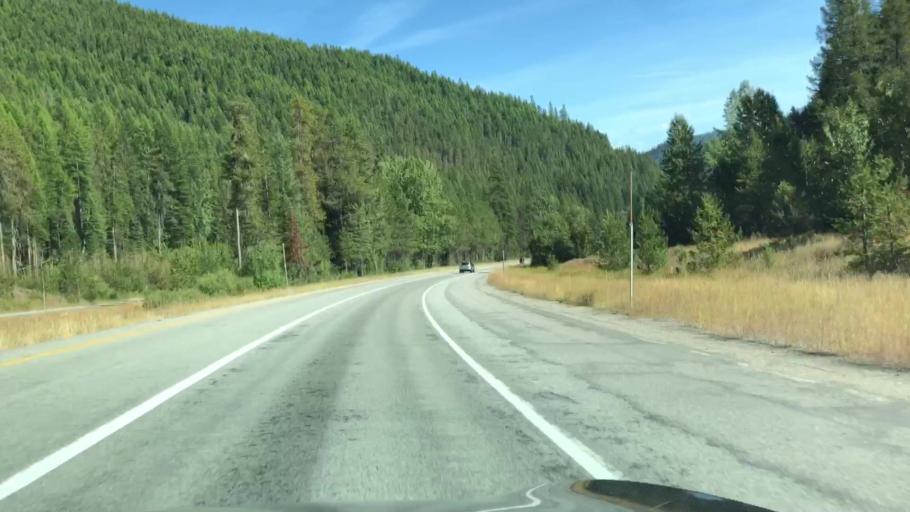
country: US
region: Idaho
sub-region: Shoshone County
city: Wallace
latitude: 47.4308
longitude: -115.6437
